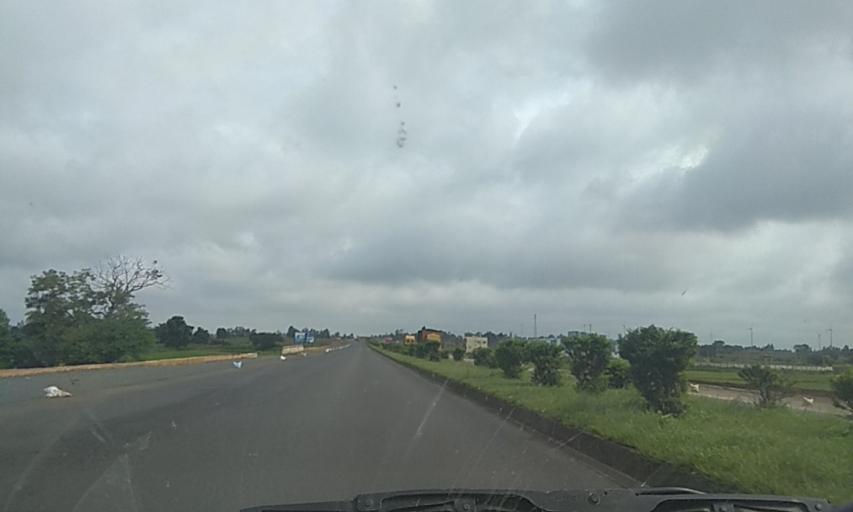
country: IN
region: Karnataka
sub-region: Haveri
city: Shiggaon
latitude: 15.0908
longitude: 75.1523
